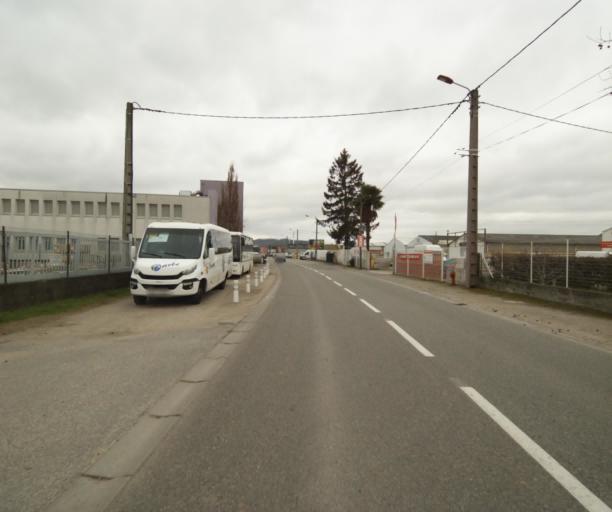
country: FR
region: Midi-Pyrenees
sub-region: Departement de l'Ariege
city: Pamiers
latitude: 43.1287
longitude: 1.6220
